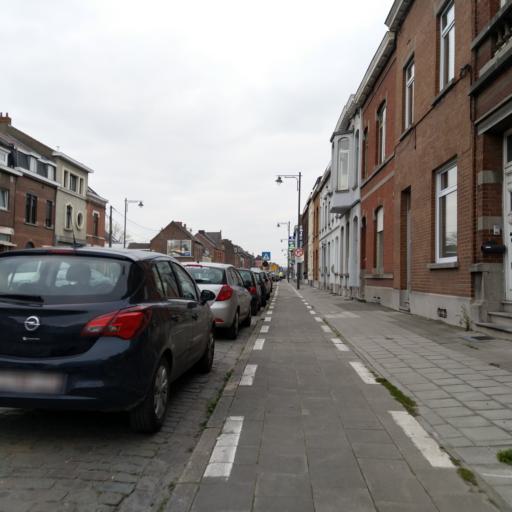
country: BE
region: Wallonia
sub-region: Province du Hainaut
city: Mons
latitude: 50.4684
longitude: 3.9573
